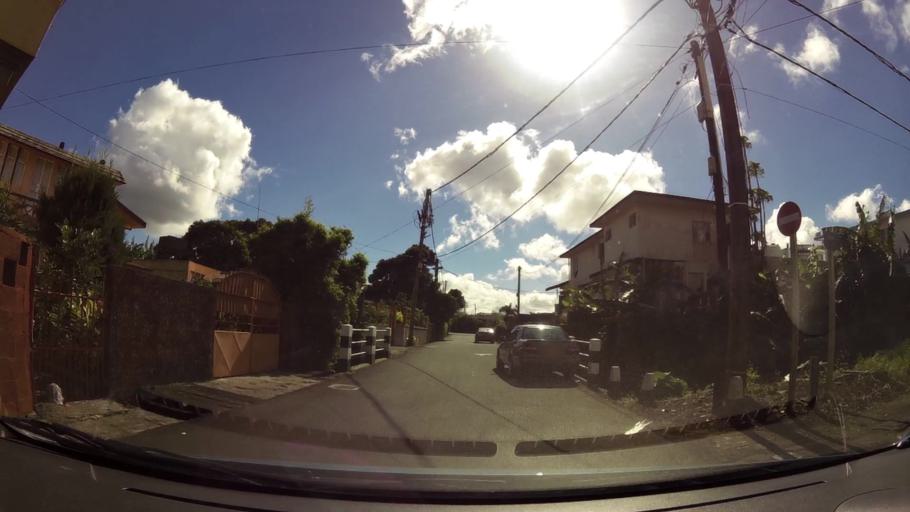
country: MU
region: Plaines Wilhems
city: Curepipe
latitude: -20.3241
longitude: 57.5328
